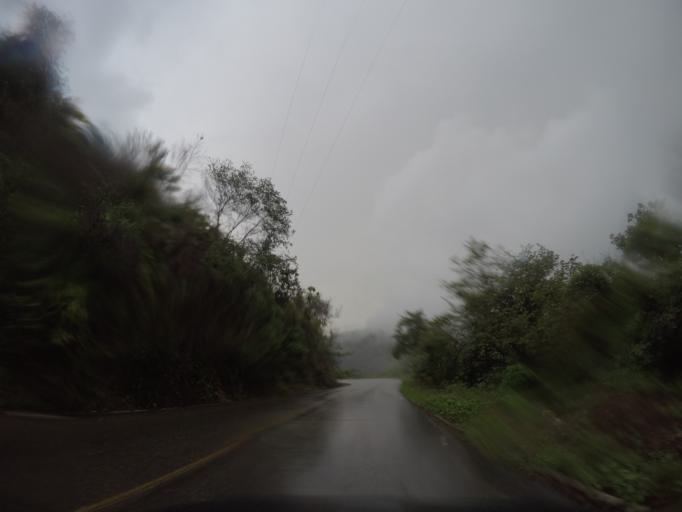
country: MX
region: Oaxaca
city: San Gabriel Mixtepec
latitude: 16.0719
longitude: -97.0783
